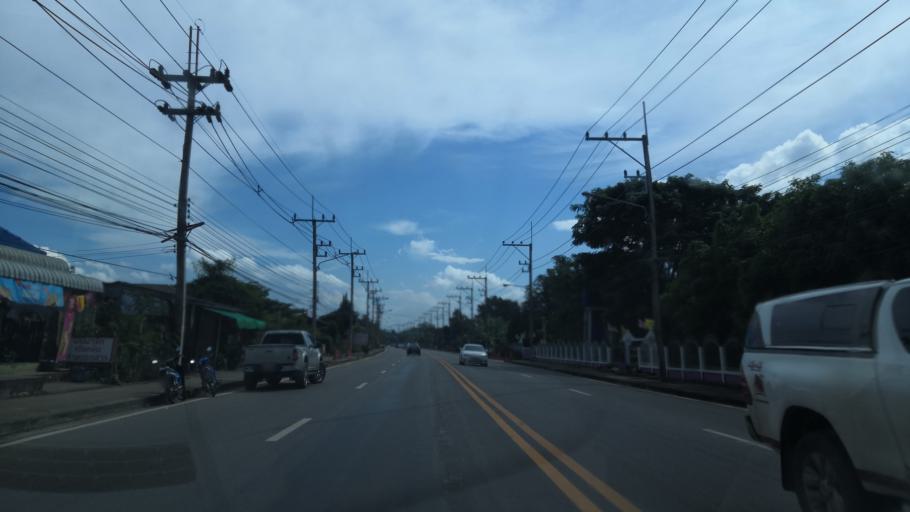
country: TH
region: Chiang Rai
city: Wiang Pa Pao
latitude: 19.2420
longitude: 99.5135
